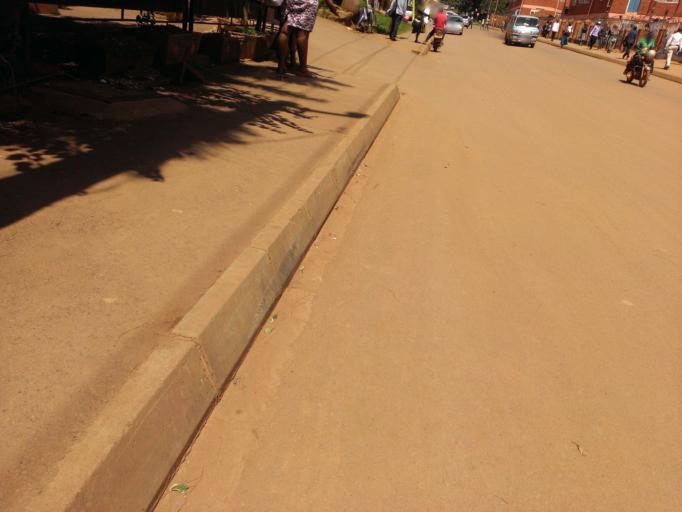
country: UG
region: Central Region
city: Kampala Central Division
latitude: 0.3292
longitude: 32.5744
